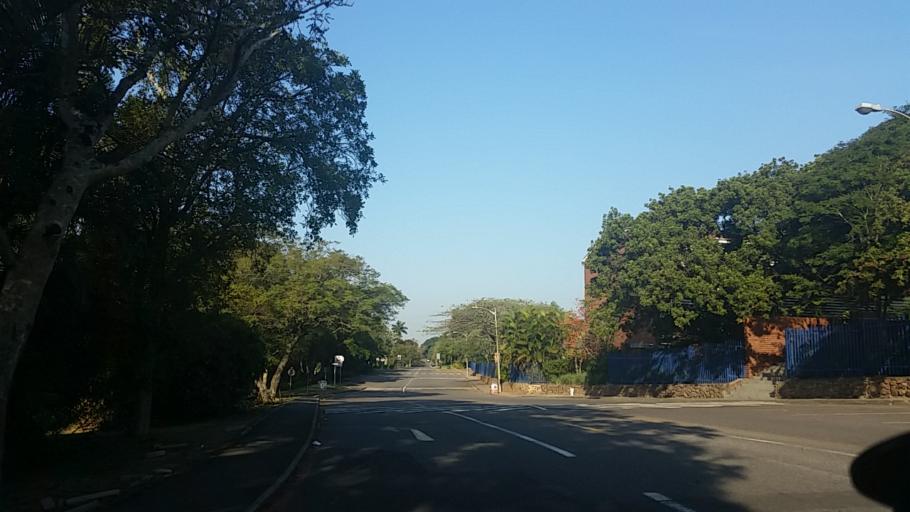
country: ZA
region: KwaZulu-Natal
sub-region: eThekwini Metropolitan Municipality
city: Berea
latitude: -29.8394
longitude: 30.9184
